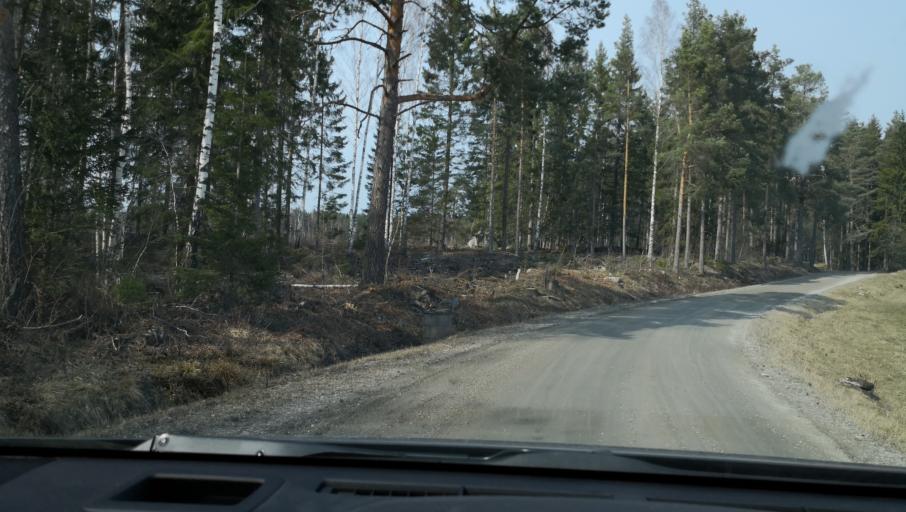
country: SE
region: OErebro
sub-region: Lindesbergs Kommun
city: Frovi
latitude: 59.3562
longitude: 15.4341
